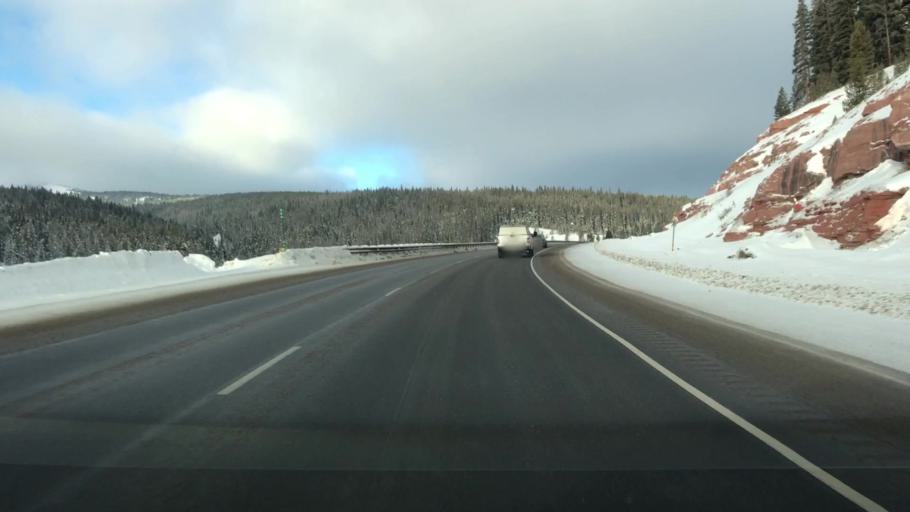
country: US
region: Colorado
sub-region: Summit County
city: Frisco
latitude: 39.5064
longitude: -106.1974
